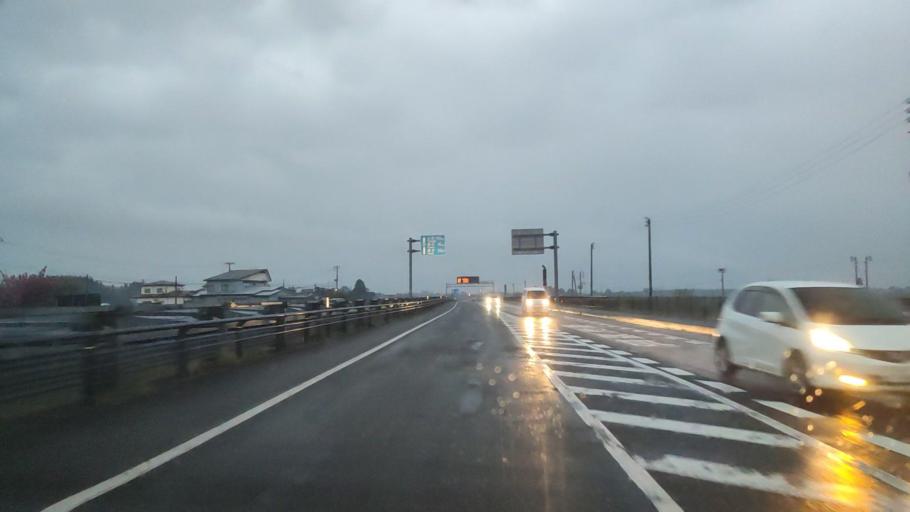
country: JP
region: Akita
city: Omagari
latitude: 39.4986
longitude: 140.4325
